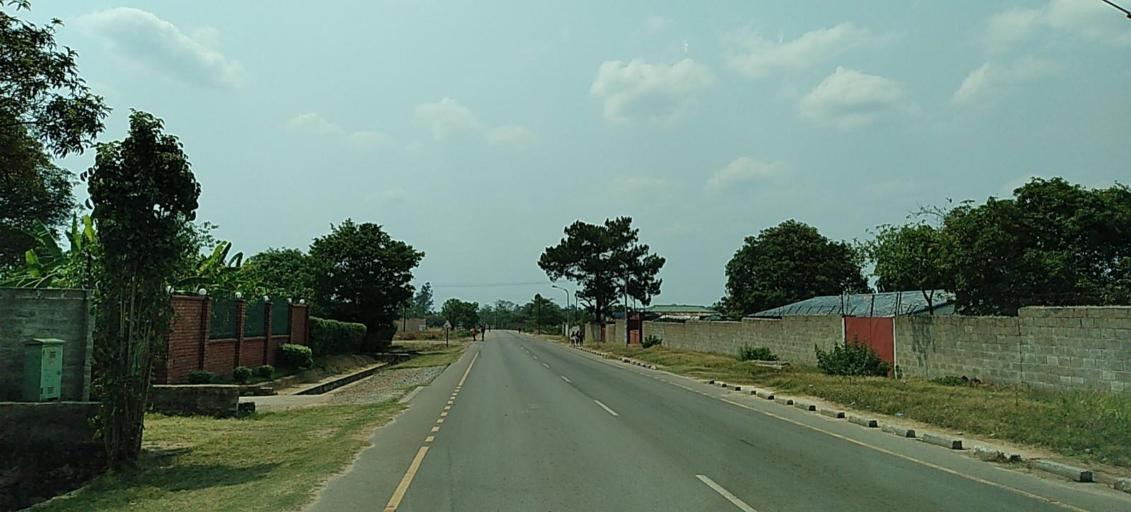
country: ZM
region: Copperbelt
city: Chambishi
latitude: -12.6374
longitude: 28.0586
